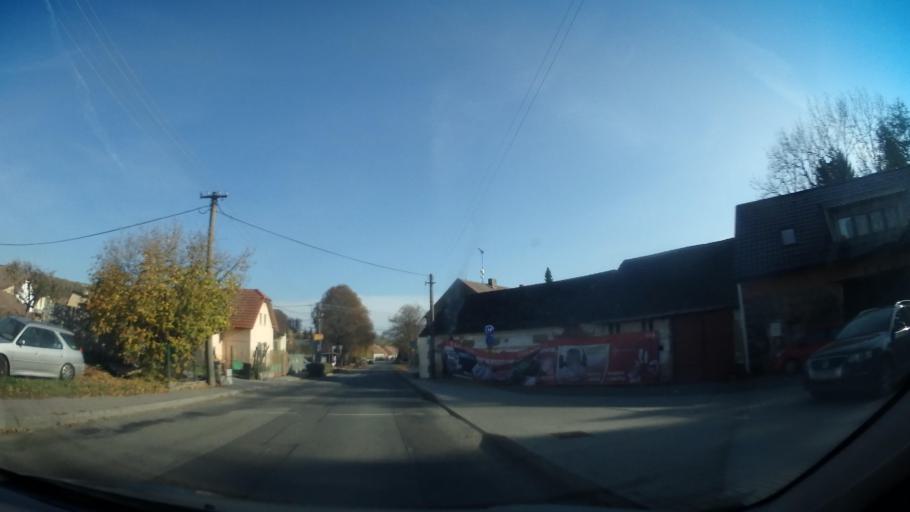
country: CZ
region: Central Bohemia
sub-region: Okres Praha-Vychod
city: Strancice
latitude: 49.9591
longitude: 14.6841
